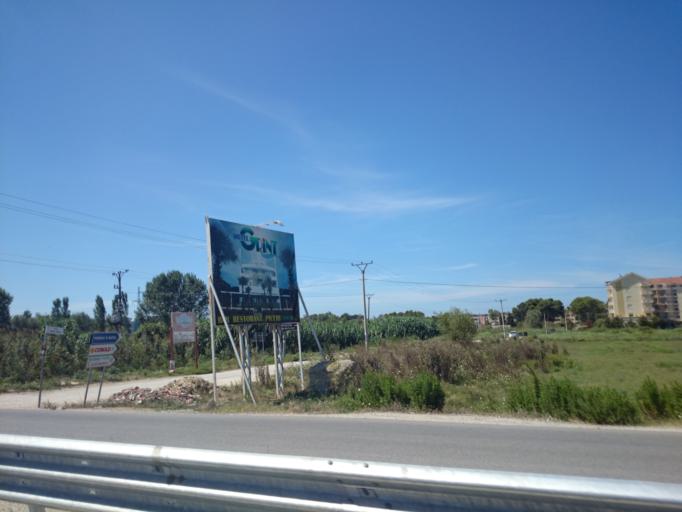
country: AL
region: Tirane
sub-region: Rrethi i Kavajes
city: Golem
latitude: 41.2422
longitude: 19.5248
